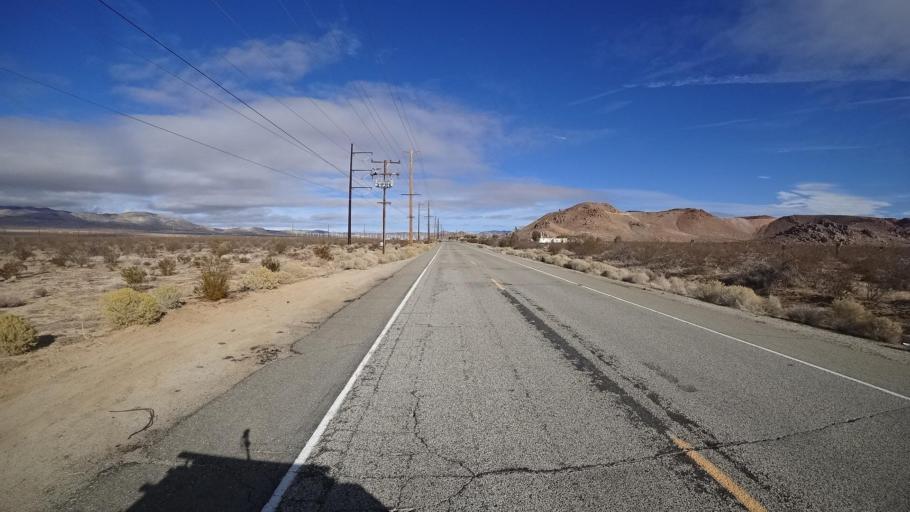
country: US
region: California
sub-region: Kern County
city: Rosamond
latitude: 34.9475
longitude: -118.2918
